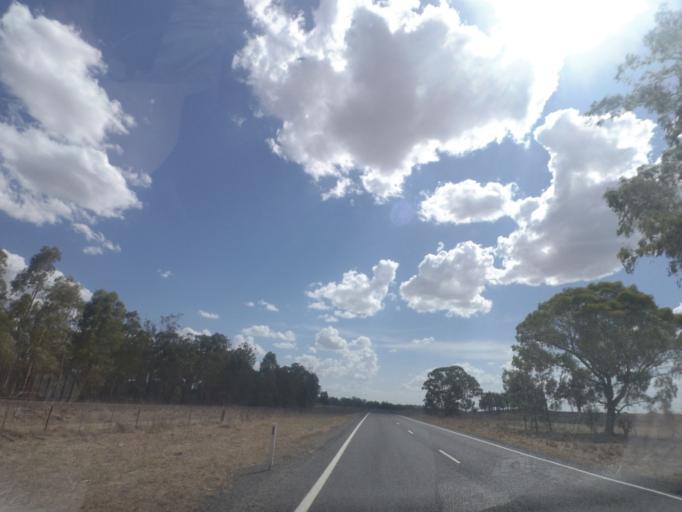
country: AU
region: Queensland
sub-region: Southern Downs
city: Stanthorpe
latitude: -28.3904
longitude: 151.3223
